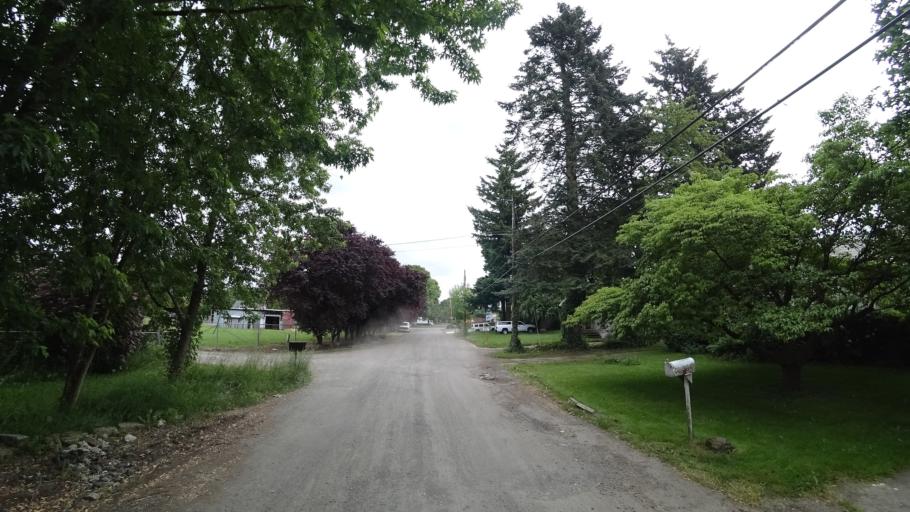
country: US
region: Oregon
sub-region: Multnomah County
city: Lents
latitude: 45.5026
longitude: -122.5700
